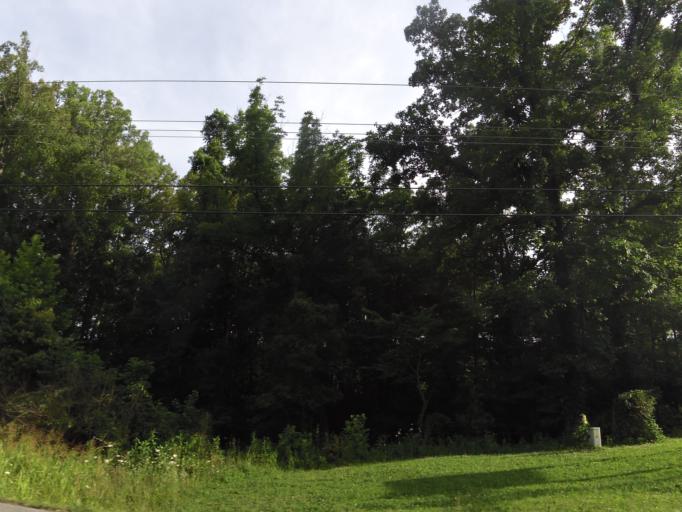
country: US
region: Tennessee
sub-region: Dickson County
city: Burns
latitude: 36.0507
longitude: -87.3200
